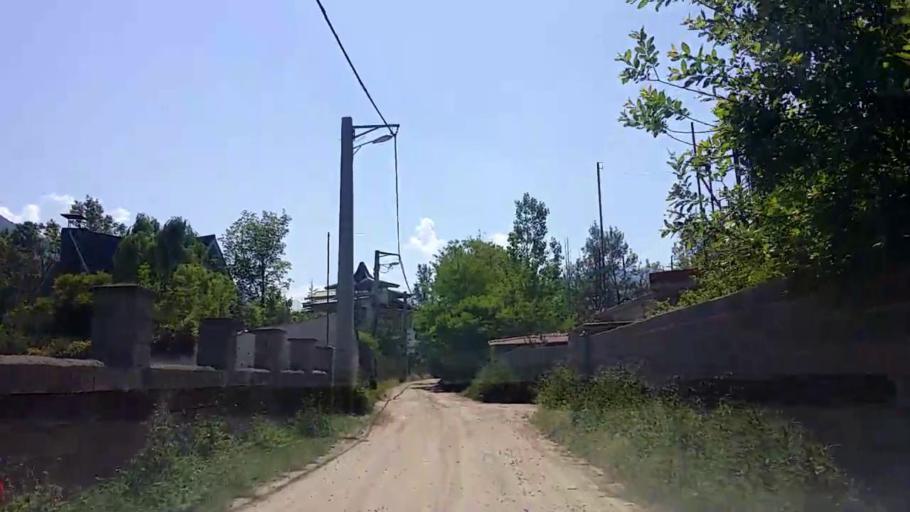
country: IR
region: Mazandaran
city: `Abbasabad
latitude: 36.5093
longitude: 51.2003
